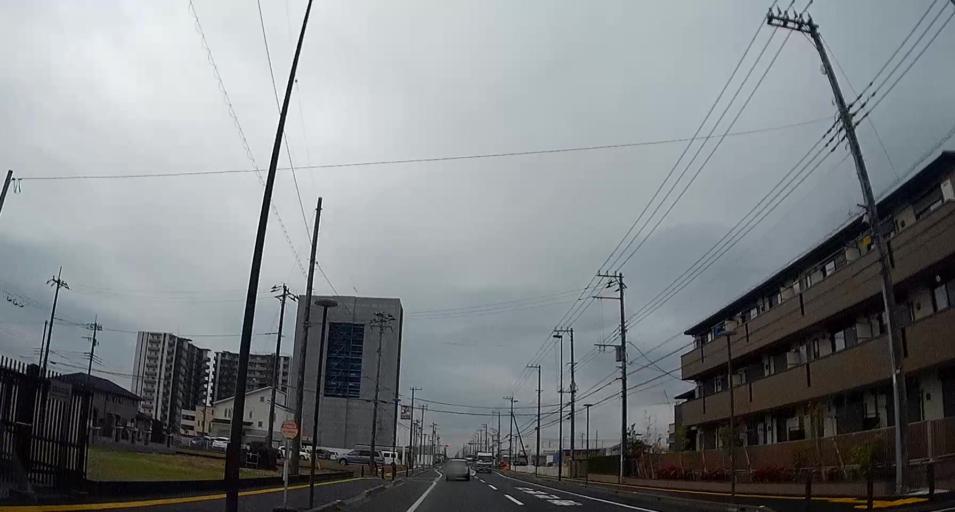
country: JP
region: Chiba
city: Kisarazu
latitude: 35.4344
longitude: 139.9586
